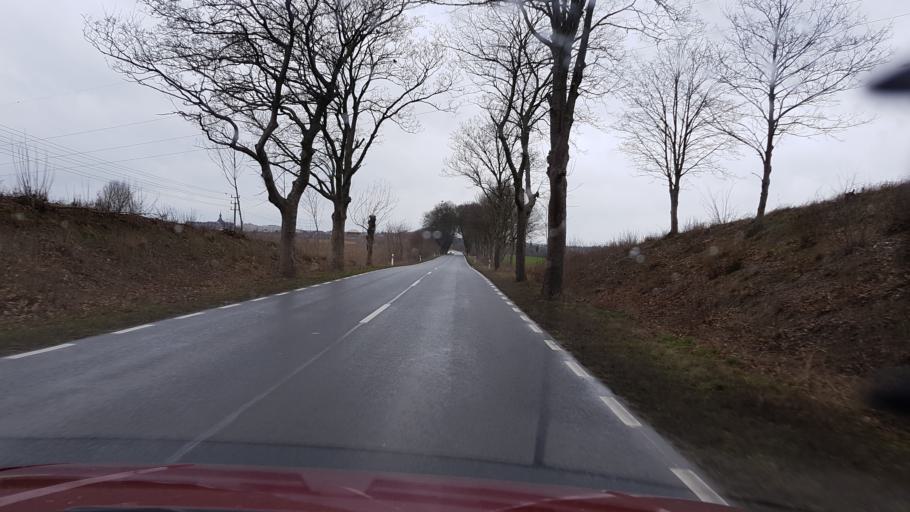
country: PL
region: West Pomeranian Voivodeship
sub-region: Powiat gryfinski
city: Gryfino
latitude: 53.2574
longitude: 14.5216
